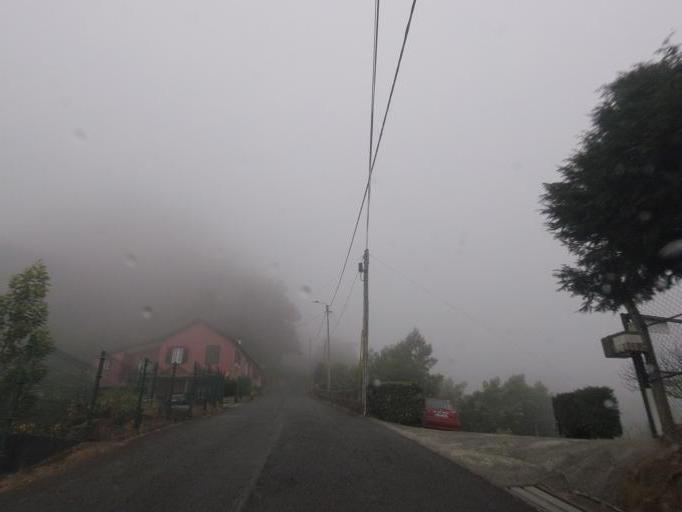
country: PT
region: Madeira
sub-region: Santa Cruz
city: Santa Cruz
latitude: 32.7282
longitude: -16.8221
